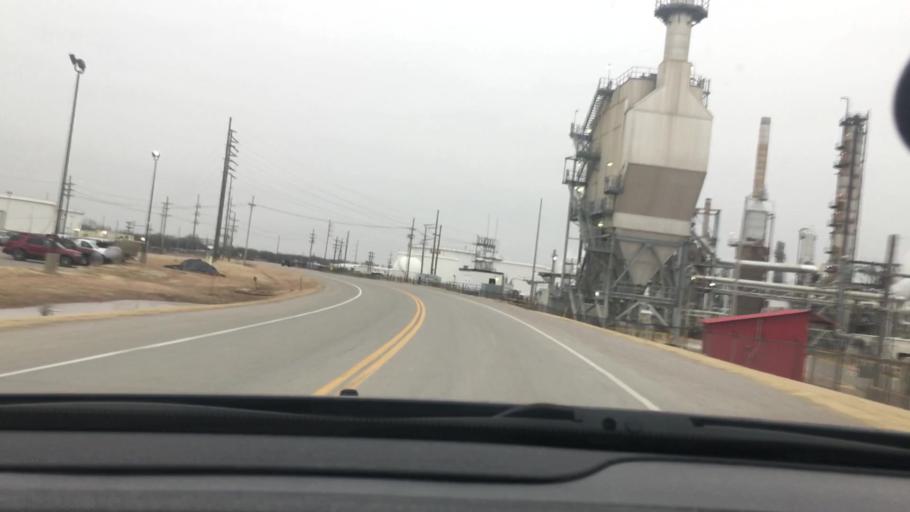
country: US
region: Oklahoma
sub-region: Garvin County
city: Wynnewood
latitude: 34.6353
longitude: -97.1689
